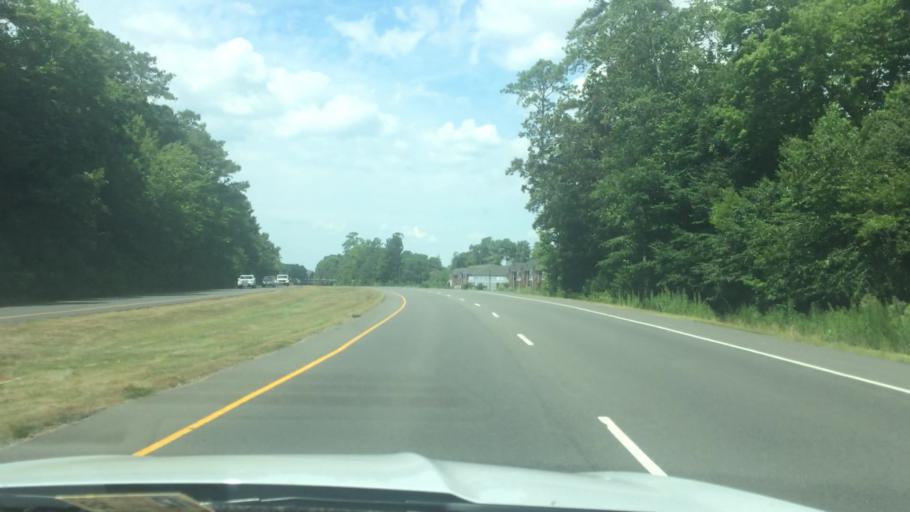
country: US
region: Virginia
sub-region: City of Poquoson
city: Poquoson
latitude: 37.1210
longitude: -76.4450
